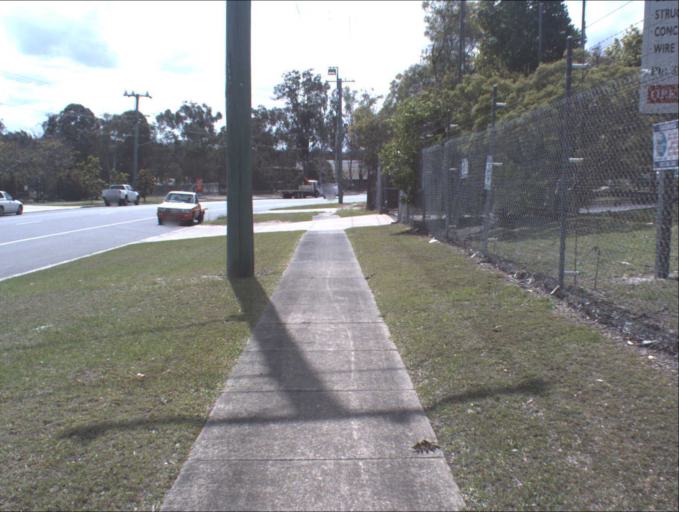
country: AU
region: Queensland
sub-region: Logan
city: Logan Reserve
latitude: -27.6798
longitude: 153.0712
